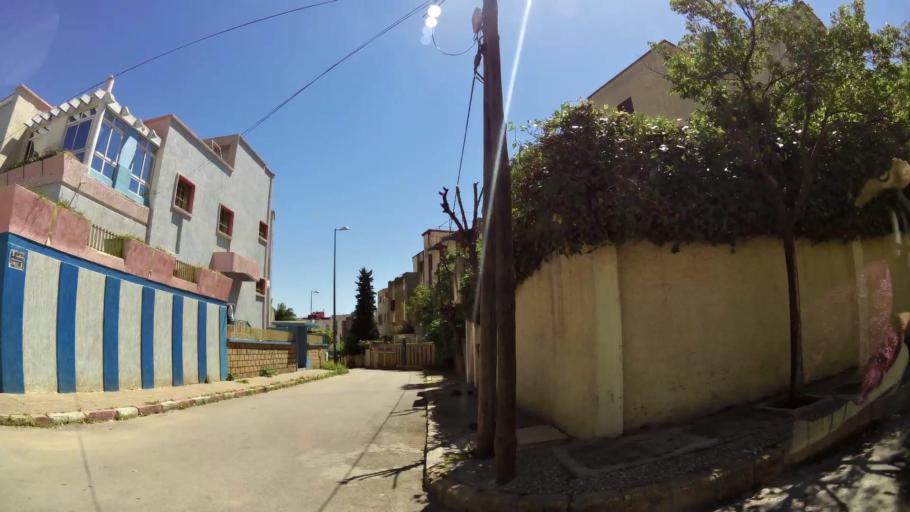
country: MA
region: Meknes-Tafilalet
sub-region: Meknes
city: Meknes
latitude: 33.9007
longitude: -5.5223
